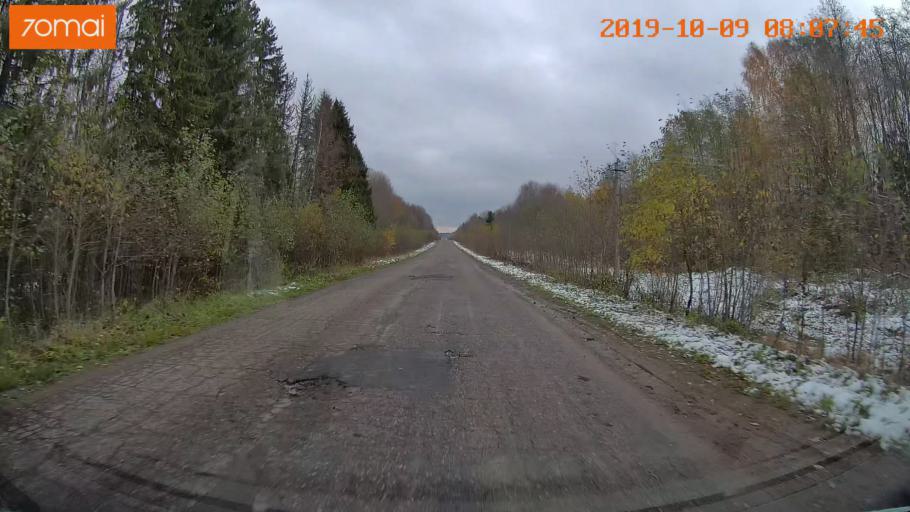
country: RU
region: Jaroslavl
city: Kukoboy
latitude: 58.6997
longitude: 40.0849
